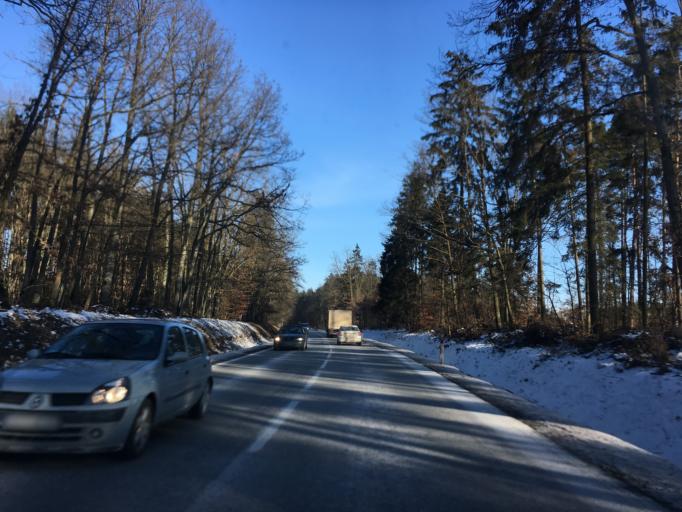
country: PL
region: Pomeranian Voivodeship
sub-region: Powiat koscierski
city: Koscierzyna
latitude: 54.1113
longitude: 17.9250
